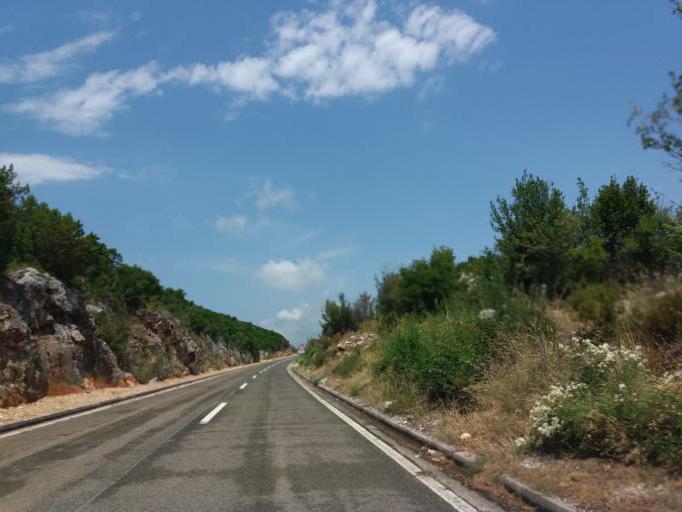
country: HR
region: Zadarska
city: Sali
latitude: 43.9969
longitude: 15.0598
